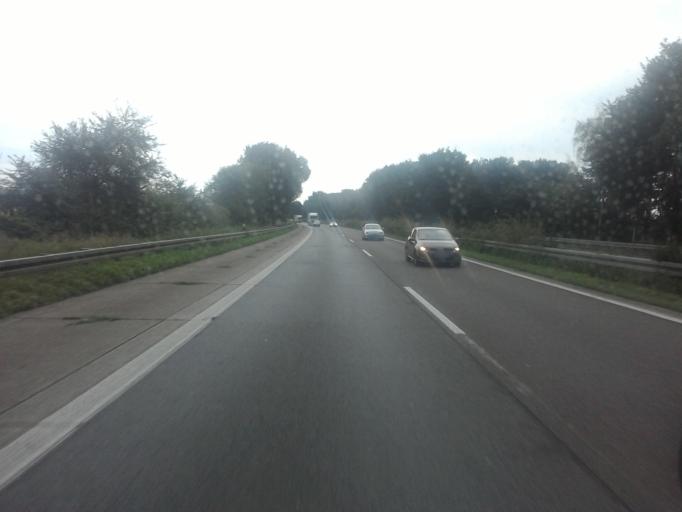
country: DE
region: North Rhine-Westphalia
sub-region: Regierungsbezirk Dusseldorf
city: Hamminkeln
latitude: 51.7160
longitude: 6.6203
